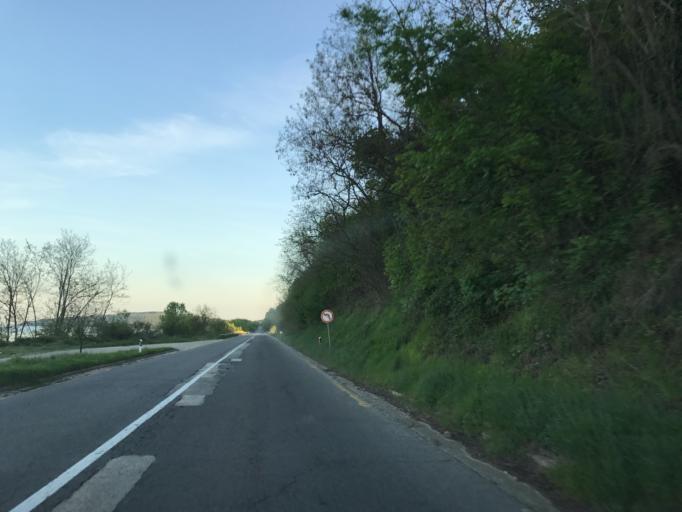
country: RO
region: Mehedinti
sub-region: Comuna Gogosu
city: Ostrovu Mare
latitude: 44.4644
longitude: 22.4506
